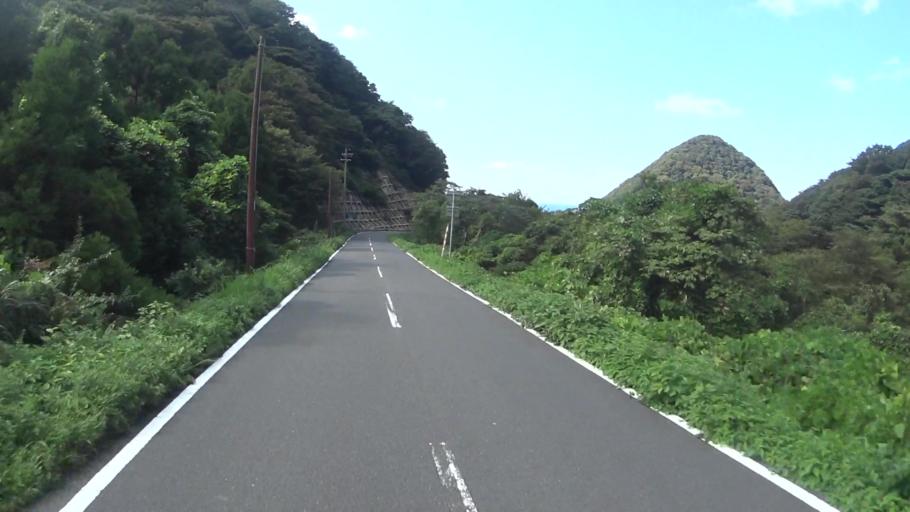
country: JP
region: Kyoto
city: Miyazu
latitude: 35.7678
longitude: 135.2260
